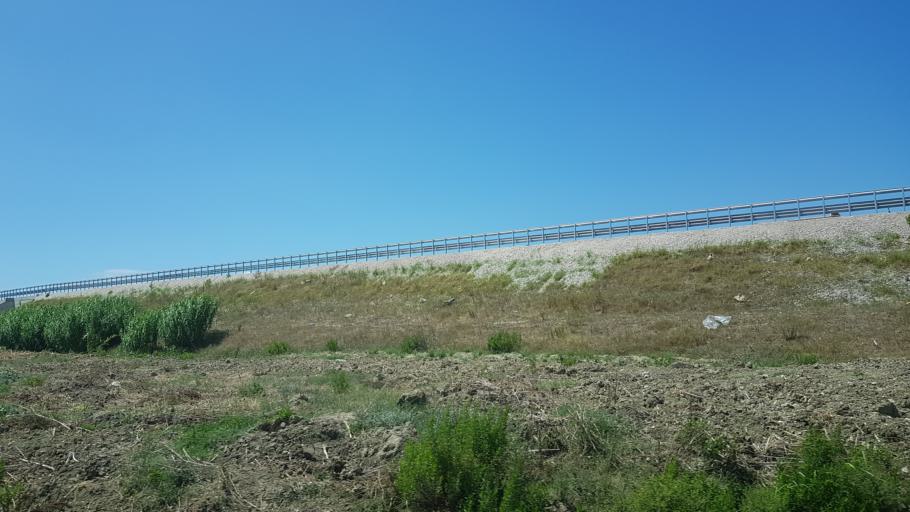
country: AL
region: Fier
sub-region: Rrethi i Fierit
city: Levan
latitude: 40.6734
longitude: 19.4799
